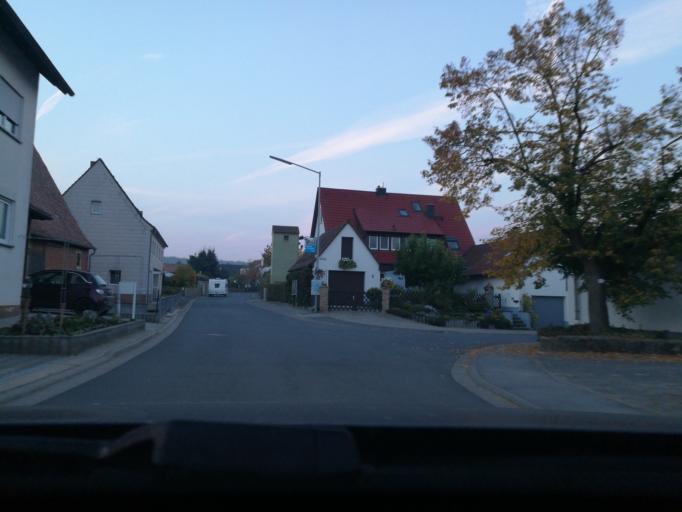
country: DE
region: Bavaria
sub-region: Regierungsbezirk Mittelfranken
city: Seukendorf
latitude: 49.4820
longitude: 10.8919
